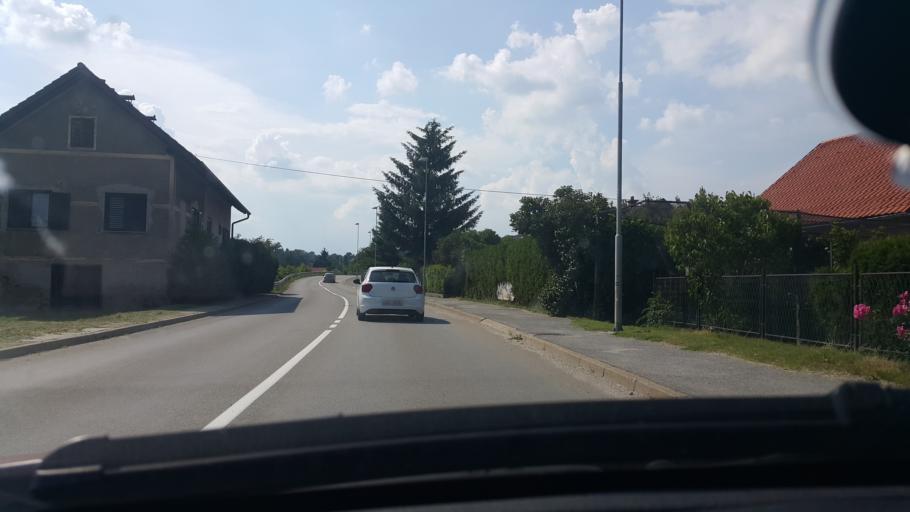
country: SI
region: Ptuj
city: Ptuj
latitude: 46.4269
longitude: 15.8893
